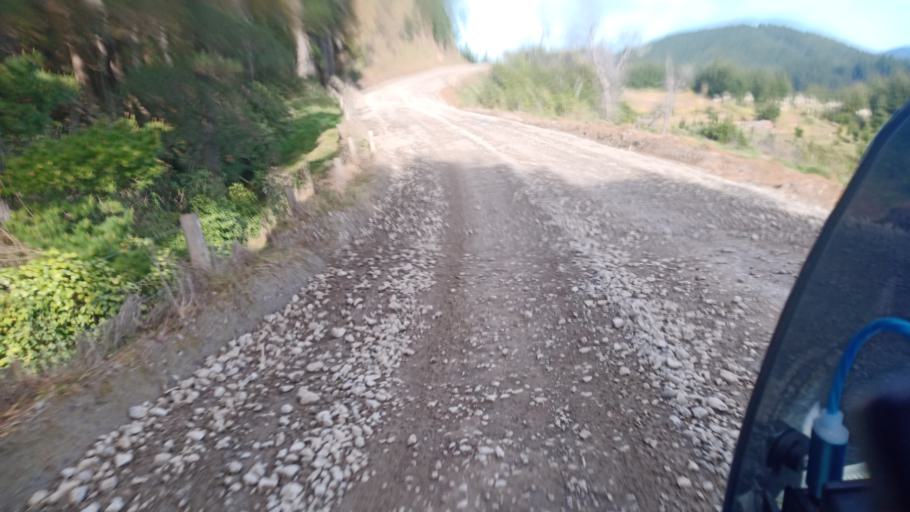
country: NZ
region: Gisborne
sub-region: Gisborne District
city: Gisborne
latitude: -38.1253
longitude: 178.1615
